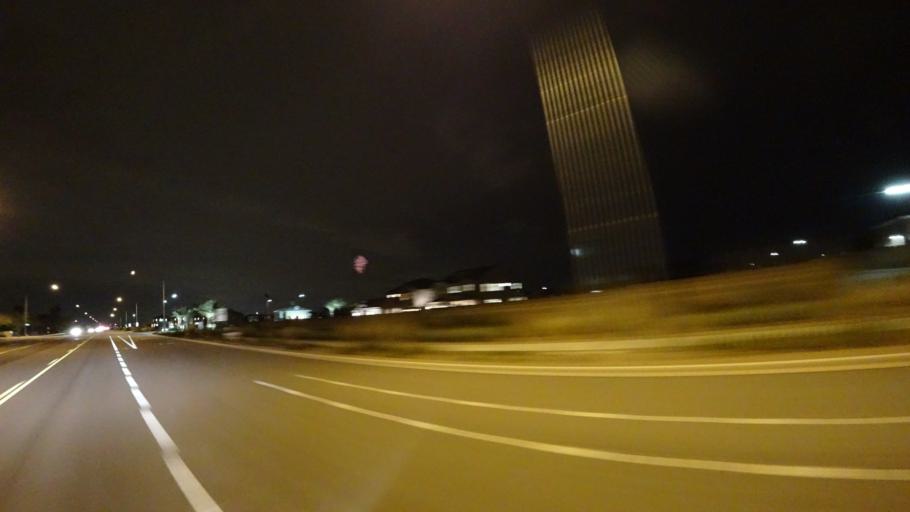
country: US
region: Arizona
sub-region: Pinal County
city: Apache Junction
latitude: 33.3645
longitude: -111.6048
